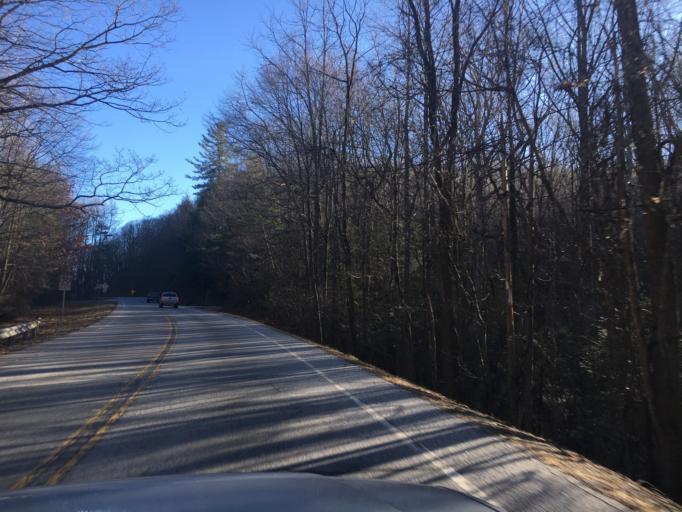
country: US
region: Georgia
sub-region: Union County
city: Blairsville
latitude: 34.7421
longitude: -83.9210
